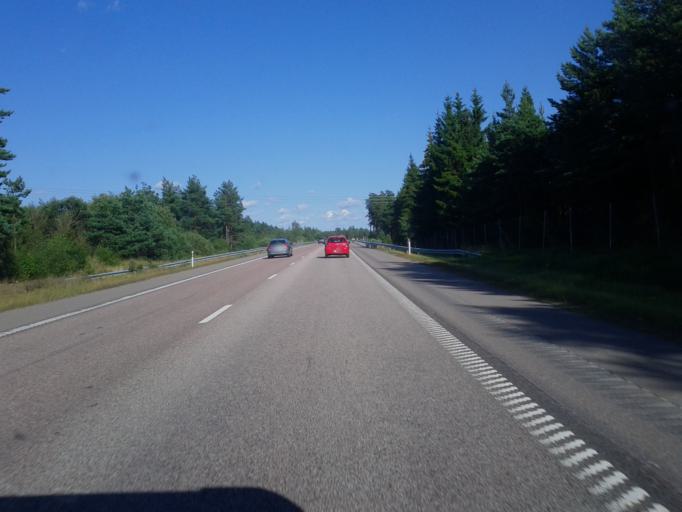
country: SE
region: Uppsala
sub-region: Enkopings Kommun
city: Grillby
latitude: 59.6446
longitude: 17.1910
